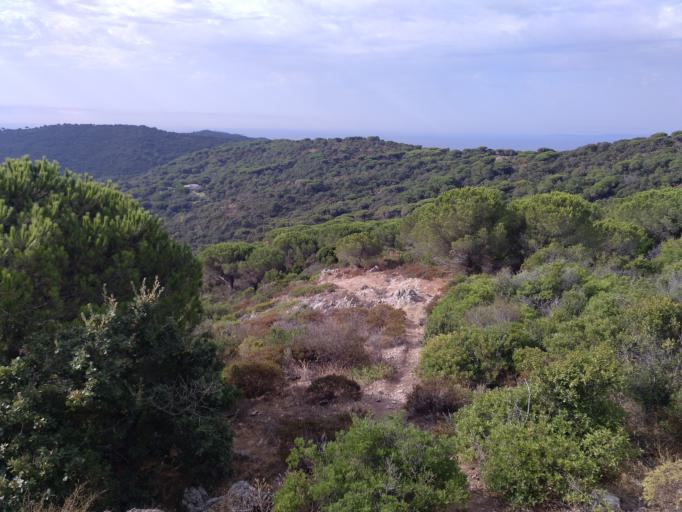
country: FR
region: Provence-Alpes-Cote d'Azur
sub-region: Departement du Var
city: Ramatuelle
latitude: 43.2077
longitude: 6.6070
